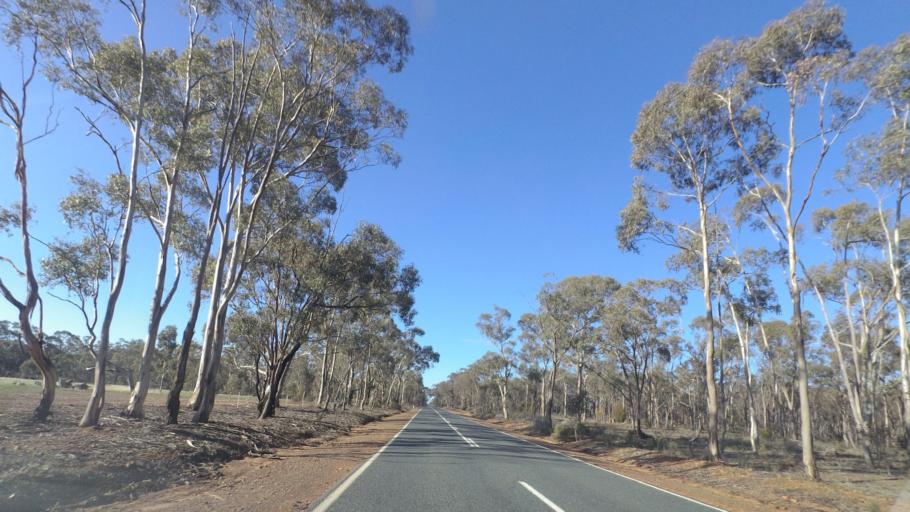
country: AU
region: Victoria
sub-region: Greater Bendigo
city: Epsom
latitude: -36.6695
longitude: 144.4215
